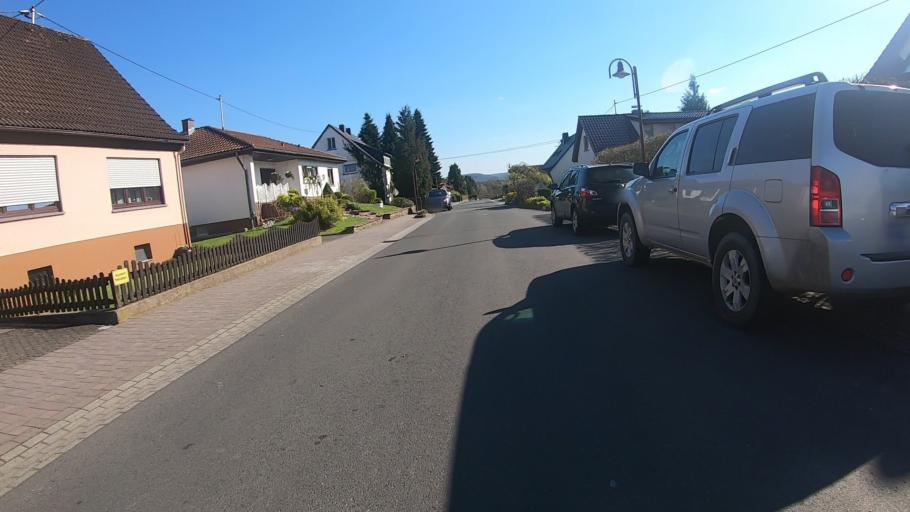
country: DE
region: Rheinland-Pfalz
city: Ruckeroth
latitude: 50.5578
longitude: 7.7444
